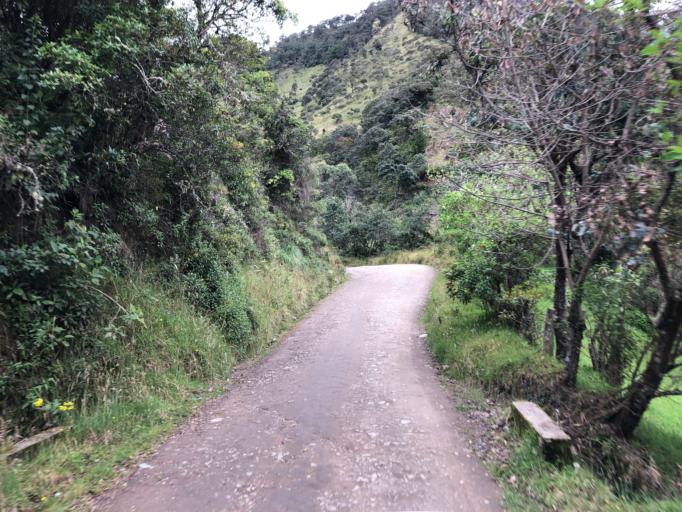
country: CO
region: Cauca
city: Totoro
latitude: 2.5087
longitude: -76.3620
